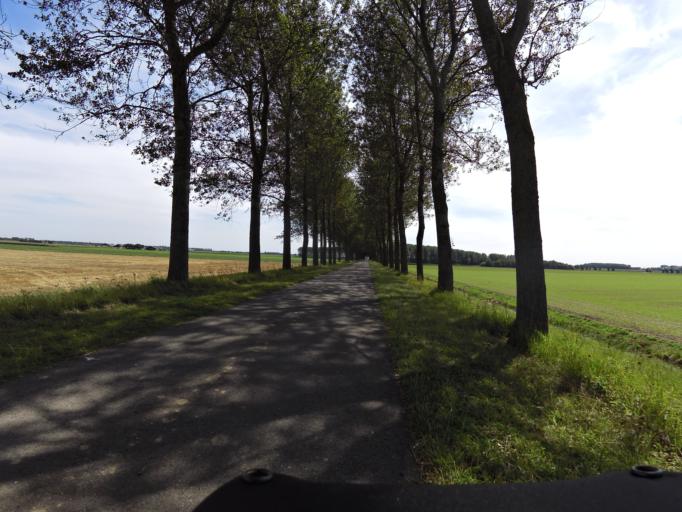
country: NL
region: South Holland
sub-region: Gemeente Goeree-Overflakkee
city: Dirksland
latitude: 51.7948
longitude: 4.0590
